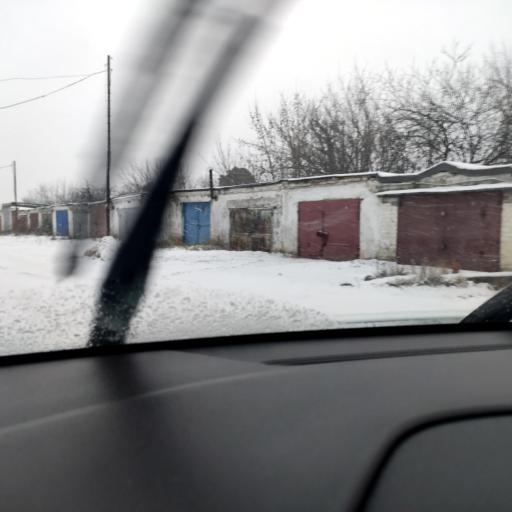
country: RU
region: Tatarstan
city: Staroye Arakchino
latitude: 55.8437
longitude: 49.0300
